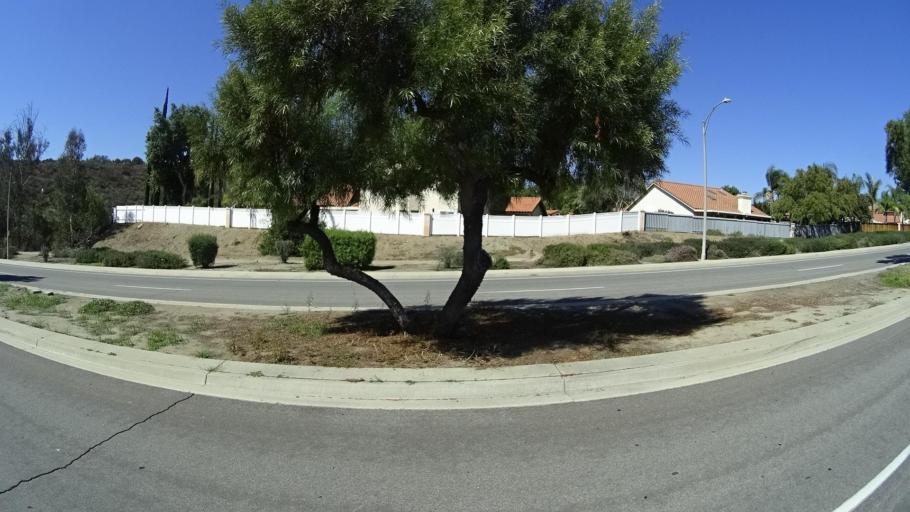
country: US
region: California
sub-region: San Diego County
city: Rancho San Diego
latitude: 32.7523
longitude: -116.9403
